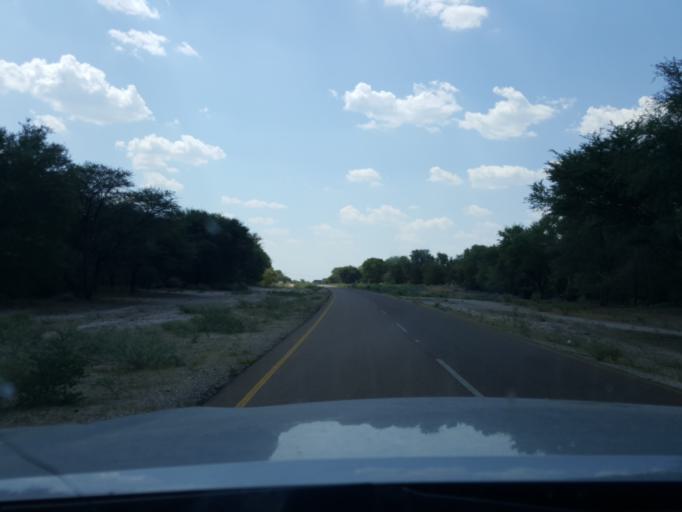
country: BW
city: Nokaneng
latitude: -19.6821
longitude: 22.1955
